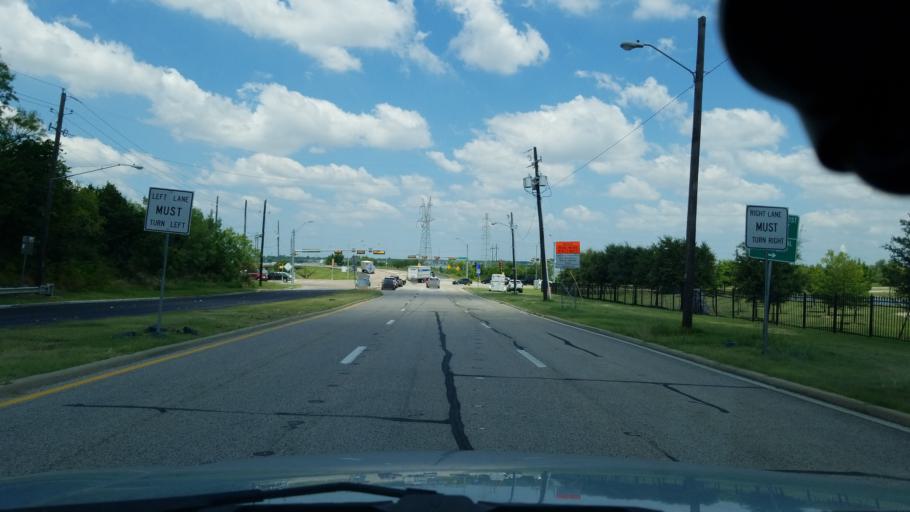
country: US
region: Texas
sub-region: Dallas County
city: Grand Prairie
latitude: 32.7063
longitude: -96.9512
